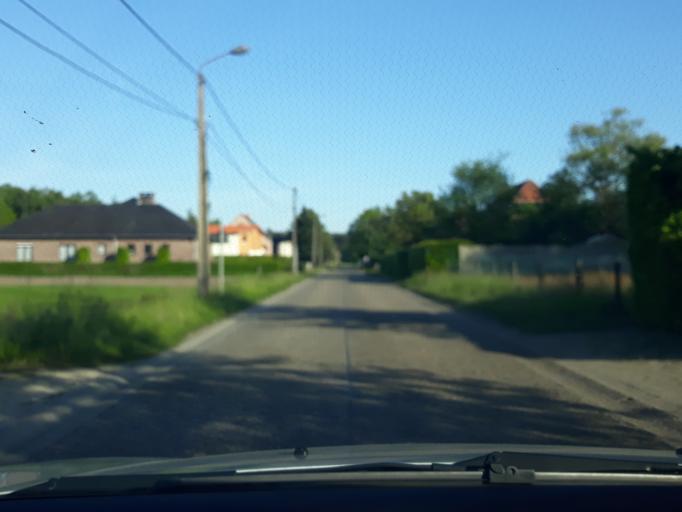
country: BE
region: Flanders
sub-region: Provincie Antwerpen
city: Vorselaar
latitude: 51.2245
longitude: 4.7530
